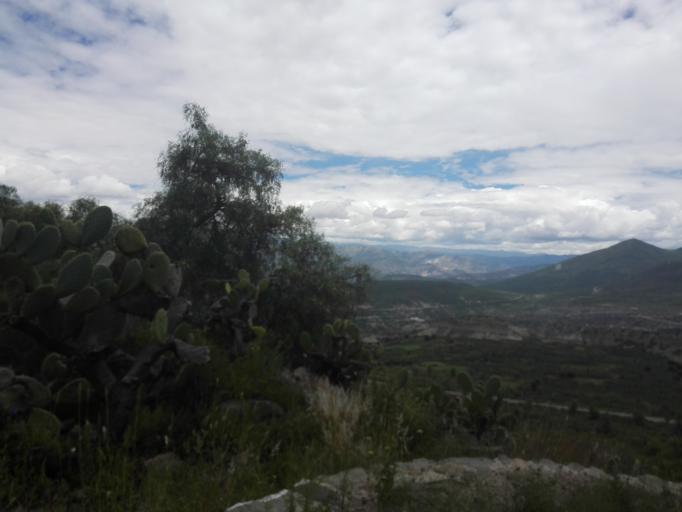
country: PE
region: Ayacucho
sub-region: Provincia de Huamanga
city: Pacaycasa
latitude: -13.0668
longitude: -74.1924
